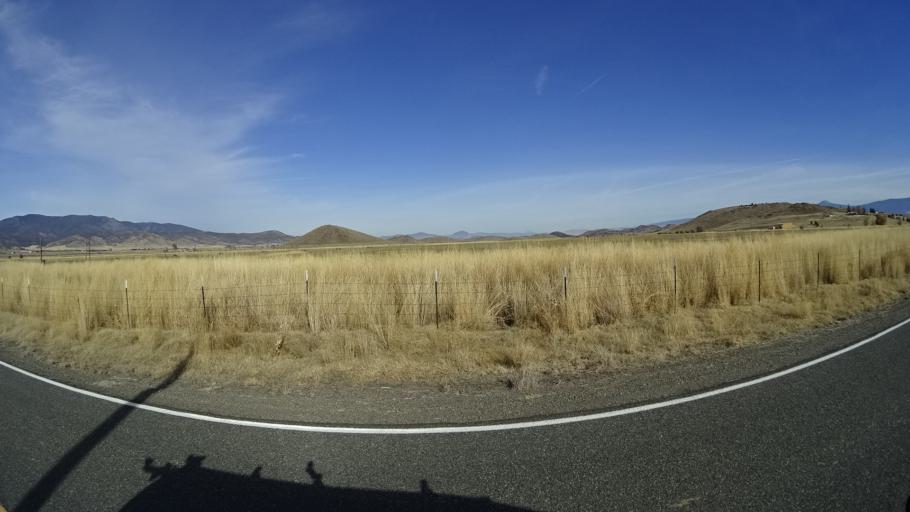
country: US
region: California
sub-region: Siskiyou County
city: Weed
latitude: 41.5345
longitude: -122.5176
